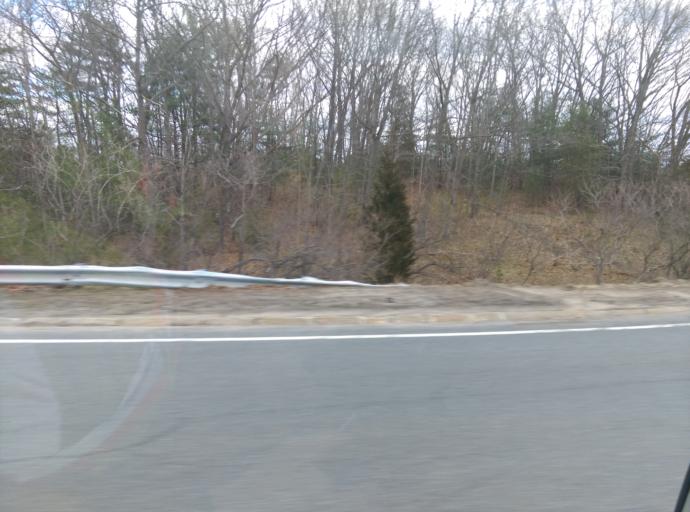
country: US
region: Massachusetts
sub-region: Essex County
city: Amesbury
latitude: 42.8387
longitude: -70.9363
